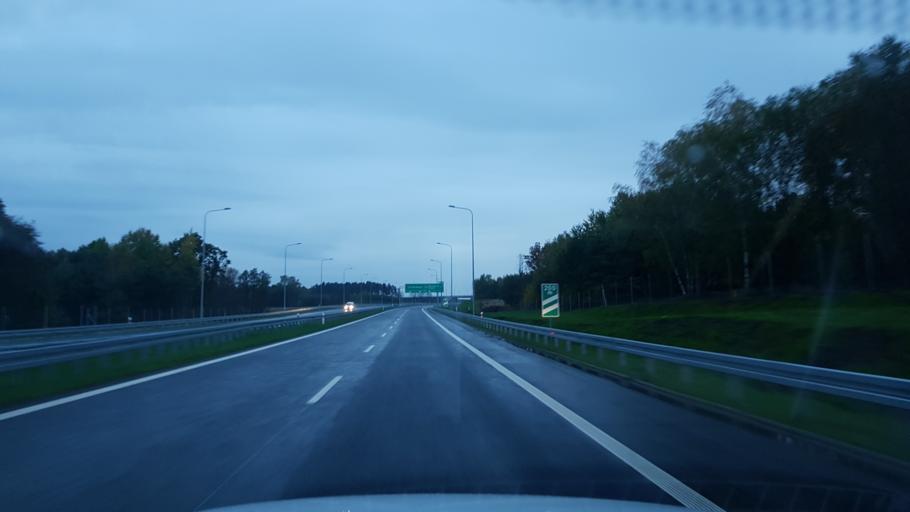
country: PL
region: West Pomeranian Voivodeship
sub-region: Powiat gryficki
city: Brojce
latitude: 53.9370
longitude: 15.3942
